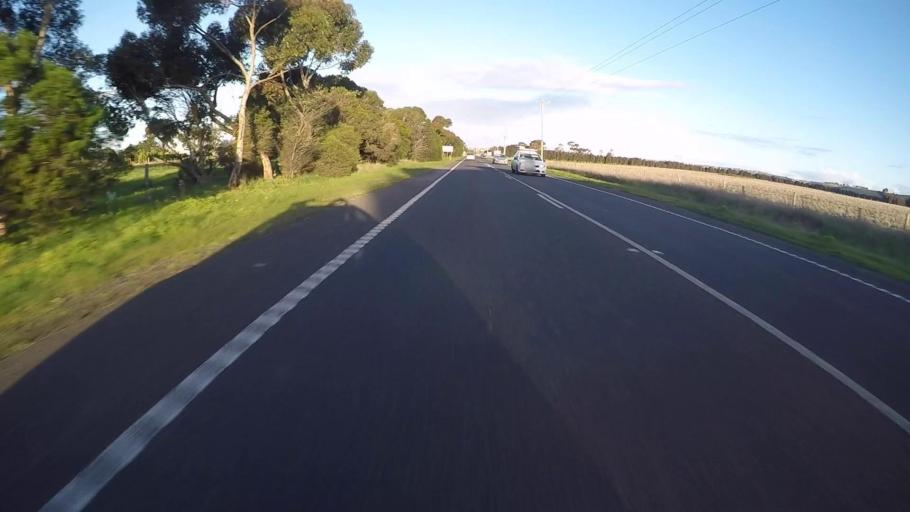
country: AU
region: Victoria
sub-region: Greater Geelong
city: Wandana Heights
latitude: -38.1361
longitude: 144.2831
